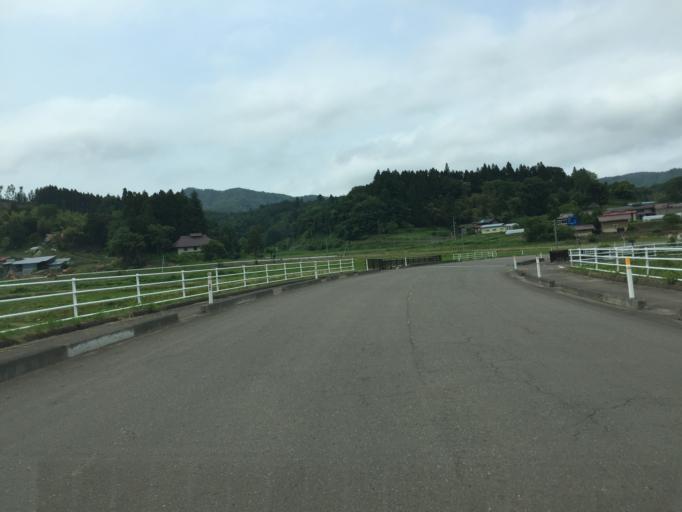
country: JP
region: Miyagi
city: Marumori
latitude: 37.8244
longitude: 140.7275
